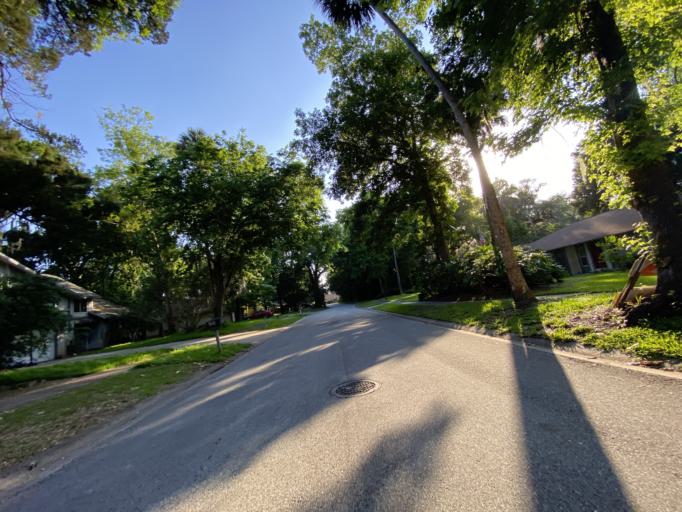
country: US
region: Florida
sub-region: Volusia County
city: Port Orange
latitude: 29.1435
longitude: -81.0094
